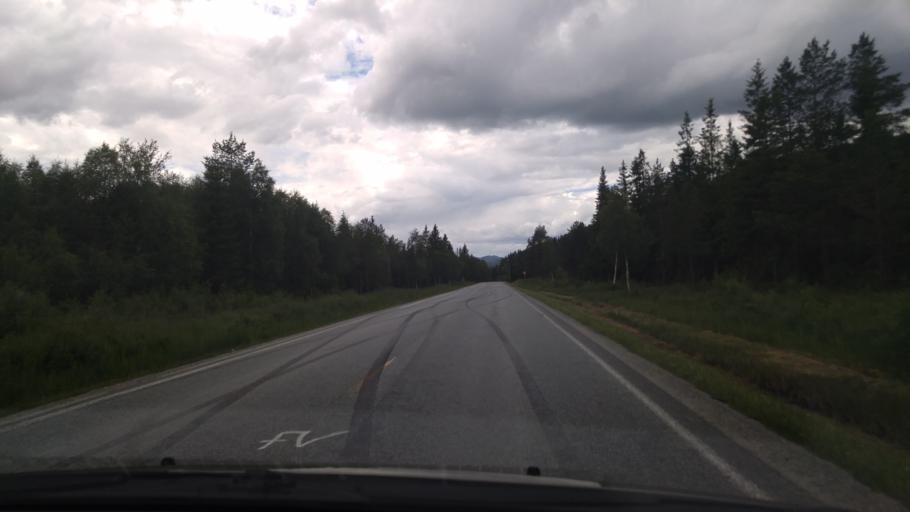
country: NO
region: Nord-Trondelag
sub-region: Steinkjer
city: Steinkjer
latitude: 64.0980
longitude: 11.4093
